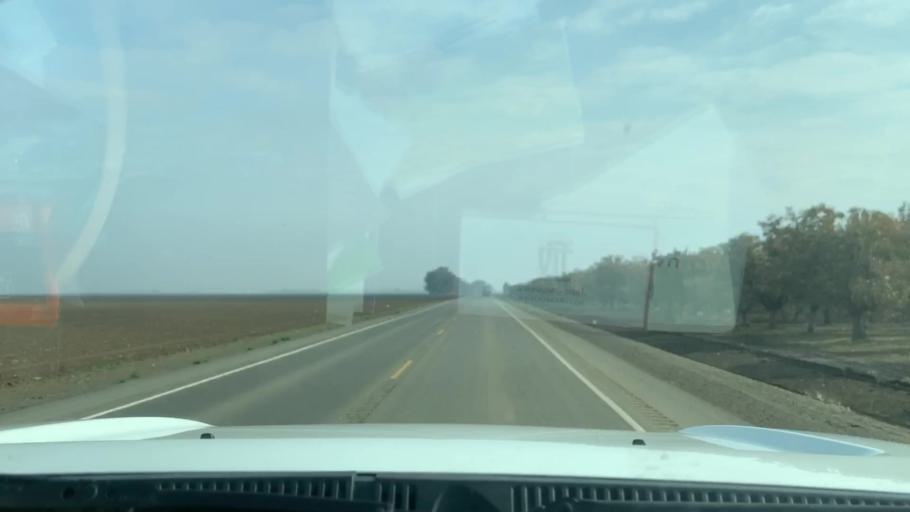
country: US
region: California
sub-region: Kings County
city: Lemoore Station
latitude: 36.2555
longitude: -119.9475
